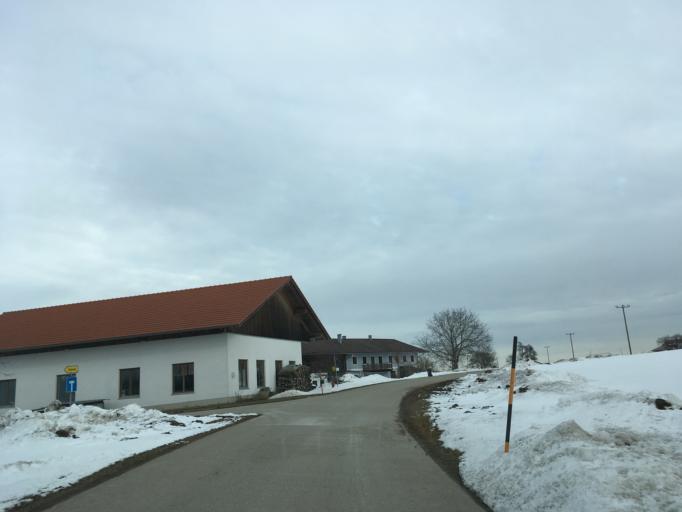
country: DE
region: Bavaria
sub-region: Upper Bavaria
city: Unterreit
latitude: 48.1001
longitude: 12.3601
